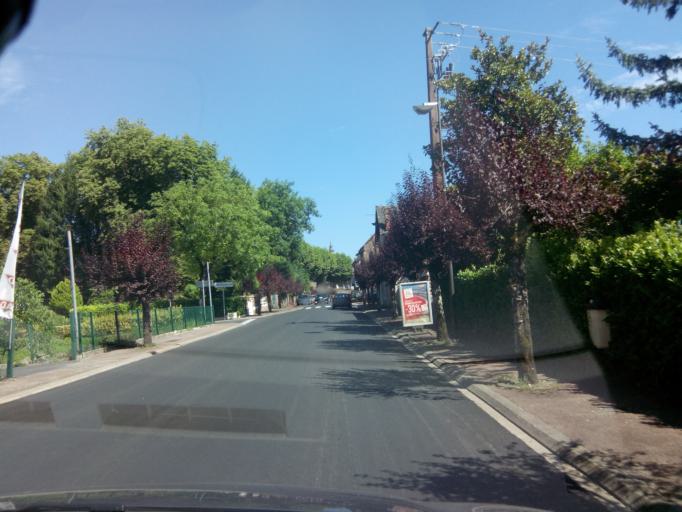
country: FR
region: Limousin
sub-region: Departement de la Correze
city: Meyssac
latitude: 45.0563
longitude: 1.6705
